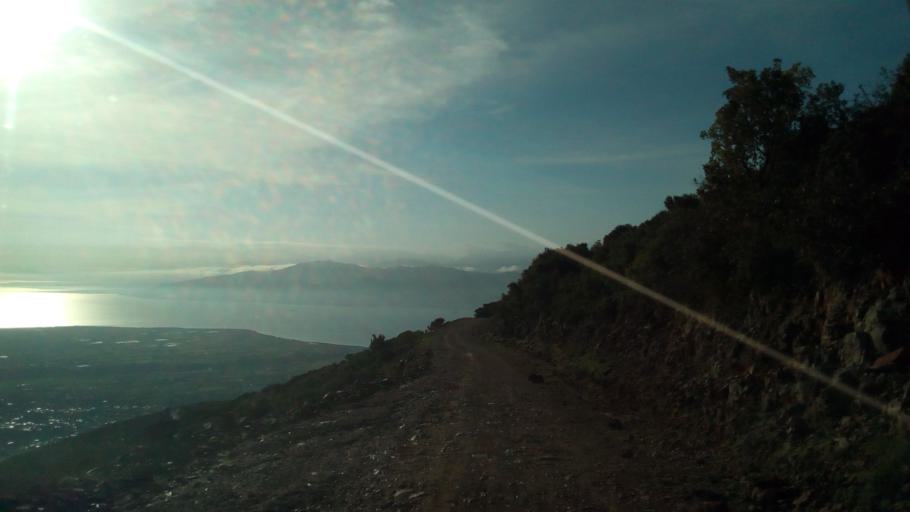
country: GR
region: West Greece
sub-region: Nomos Aitolias kai Akarnanias
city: Nafpaktos
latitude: 38.4120
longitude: 21.8229
